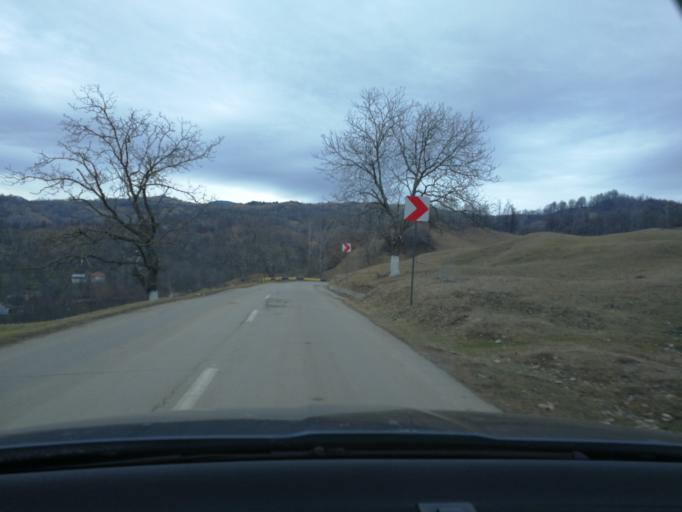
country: RO
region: Prahova
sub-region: Comuna Adunati
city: Ocina de Sus
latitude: 45.1849
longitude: 25.6129
